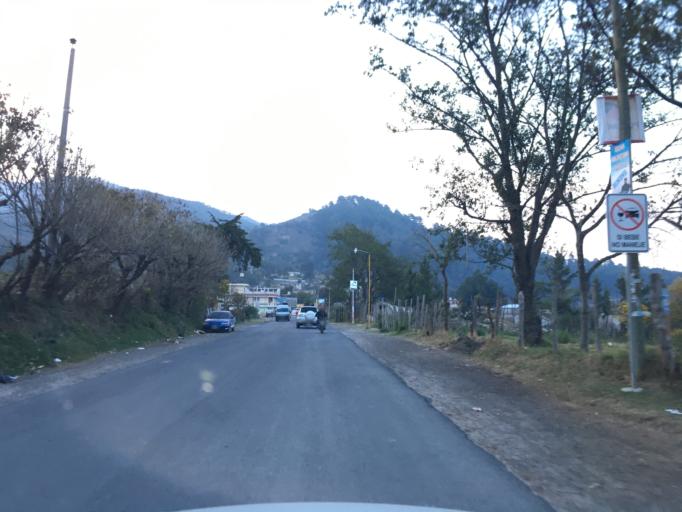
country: GT
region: Chimaltenango
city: Tecpan Guatemala
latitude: 14.7553
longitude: -90.9996
